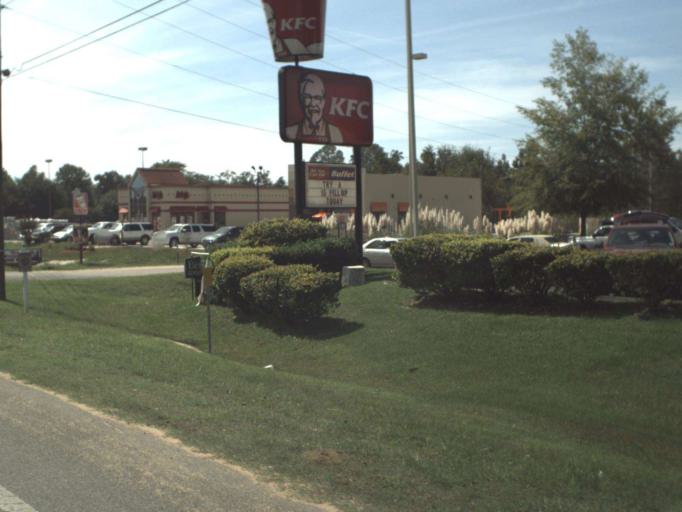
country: US
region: Florida
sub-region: Washington County
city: Chipley
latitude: 30.7554
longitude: -85.5497
